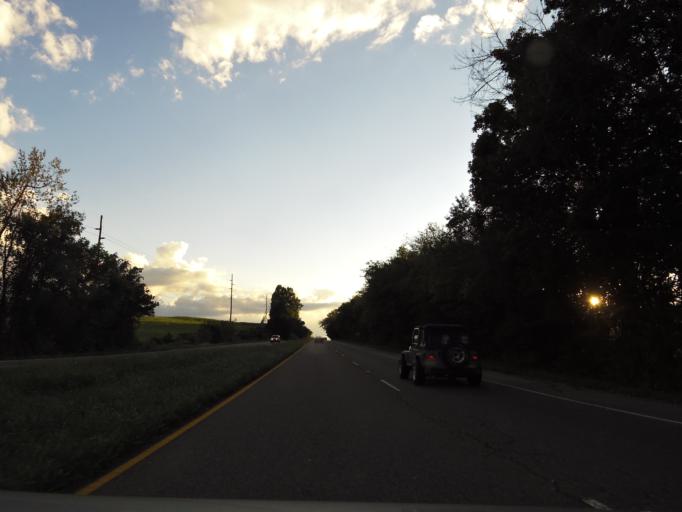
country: US
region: Tennessee
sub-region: Knox County
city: Mascot
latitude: 36.0614
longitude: -83.6844
